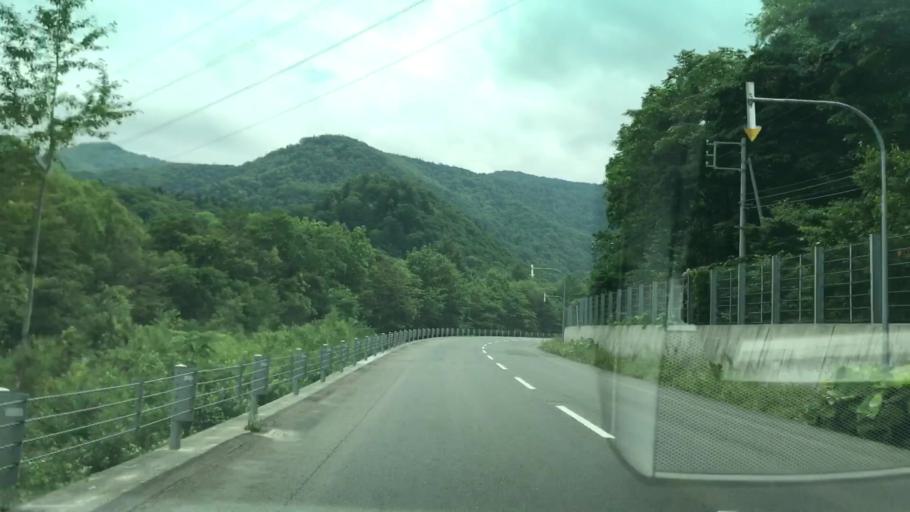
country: JP
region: Hokkaido
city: Yoichi
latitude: 43.0374
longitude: 140.8616
